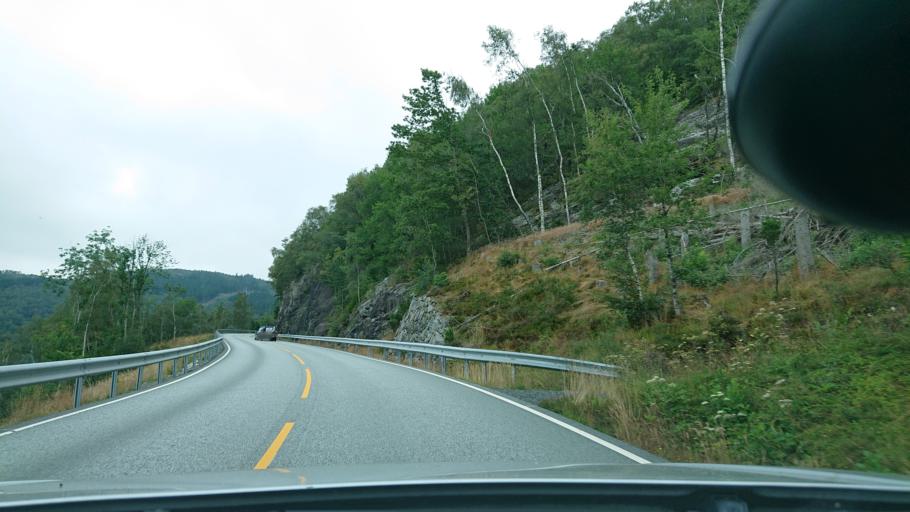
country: NO
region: Rogaland
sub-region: Hjelmeland
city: Hjelmelandsvagen
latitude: 59.1731
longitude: 6.1409
